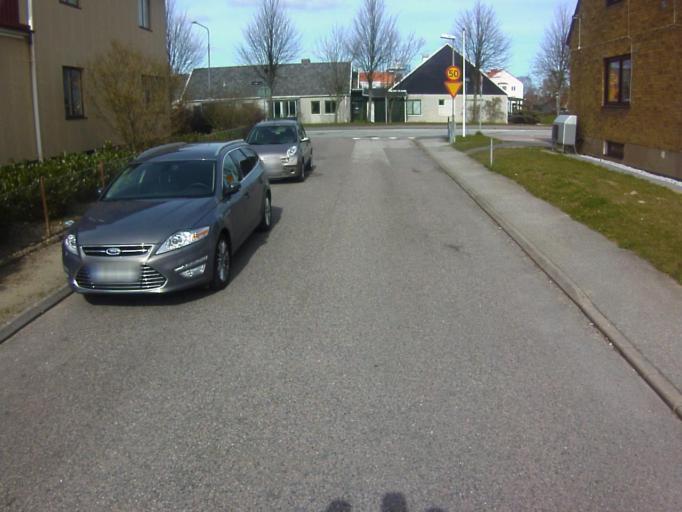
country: SE
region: Skane
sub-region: Kavlinge Kommun
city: Kaevlinge
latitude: 55.7904
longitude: 13.1187
